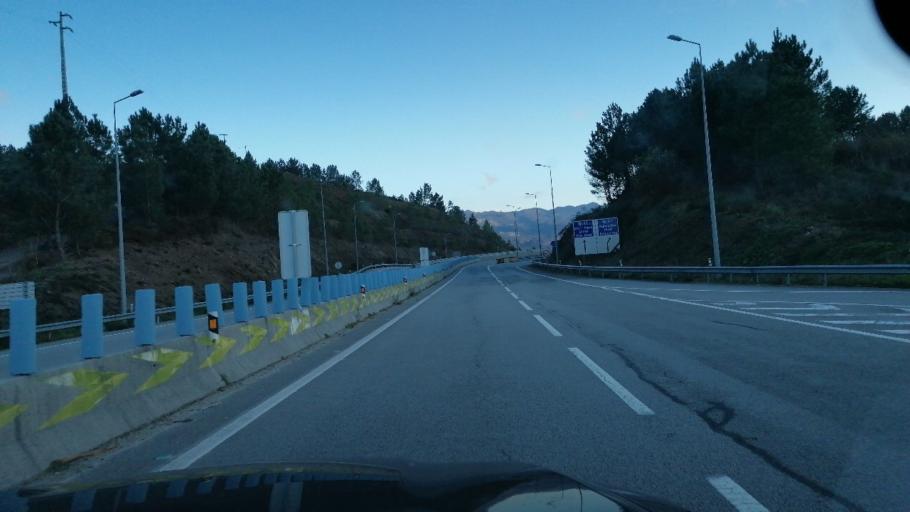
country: PT
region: Braga
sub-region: Cabeceiras de Basto
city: Cabeceiras de Basto
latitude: 41.4755
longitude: -7.9481
